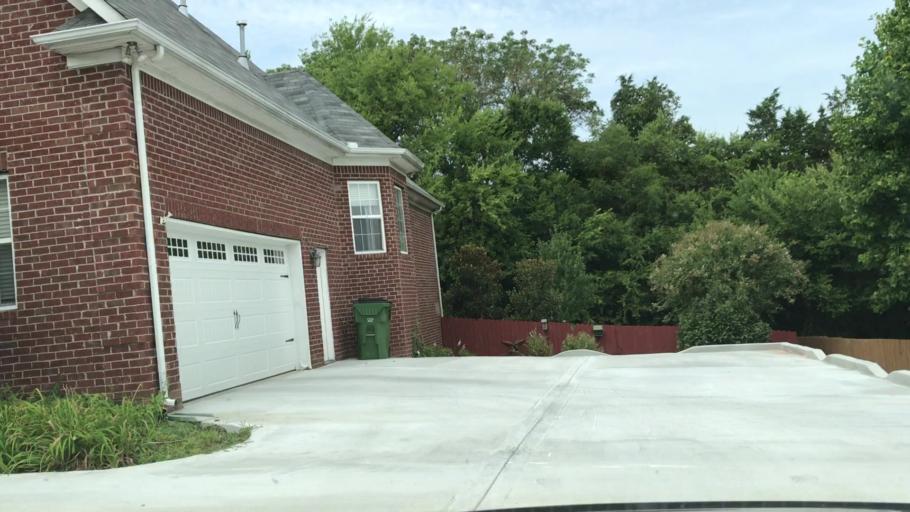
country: US
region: Tennessee
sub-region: Williamson County
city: Nolensville
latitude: 35.9620
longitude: -86.6141
